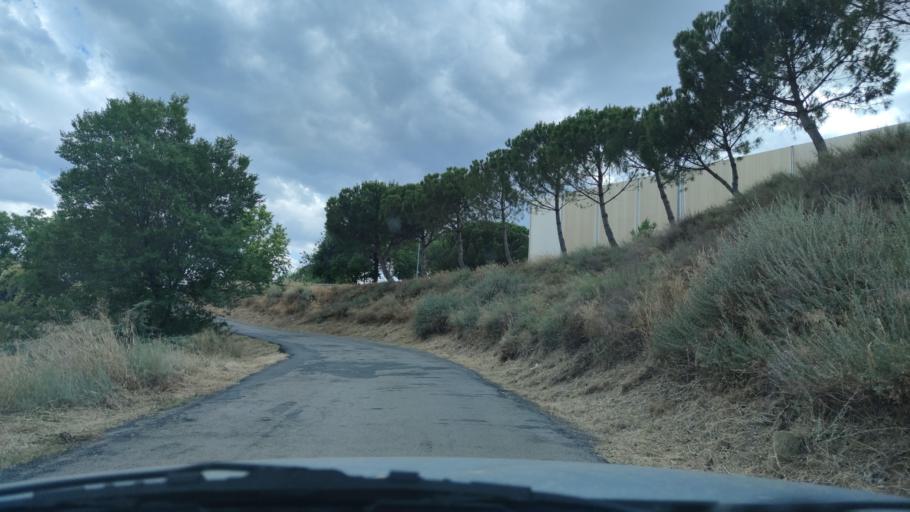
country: ES
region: Catalonia
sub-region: Provincia de Lleida
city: Lleida
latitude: 41.6013
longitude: 0.5829
